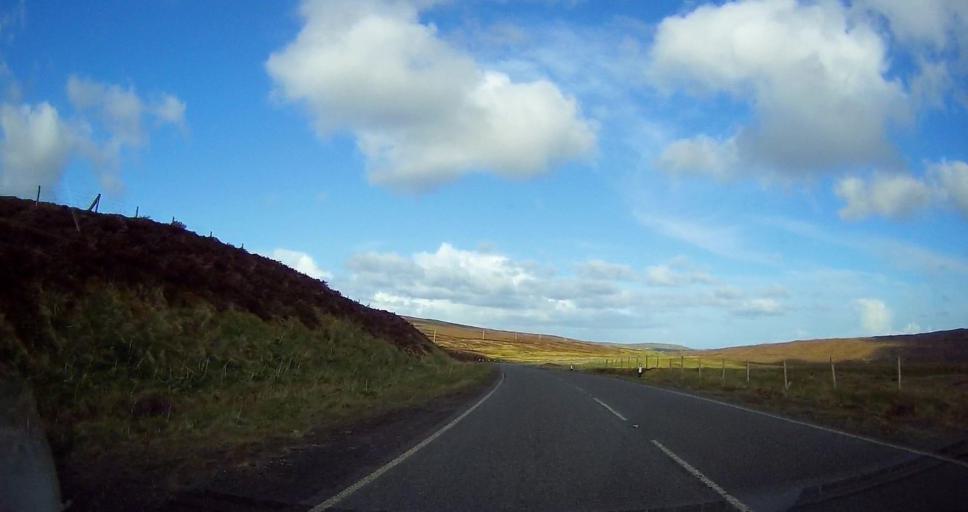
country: GB
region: Scotland
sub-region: Shetland Islands
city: Lerwick
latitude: 60.3486
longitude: -1.2229
